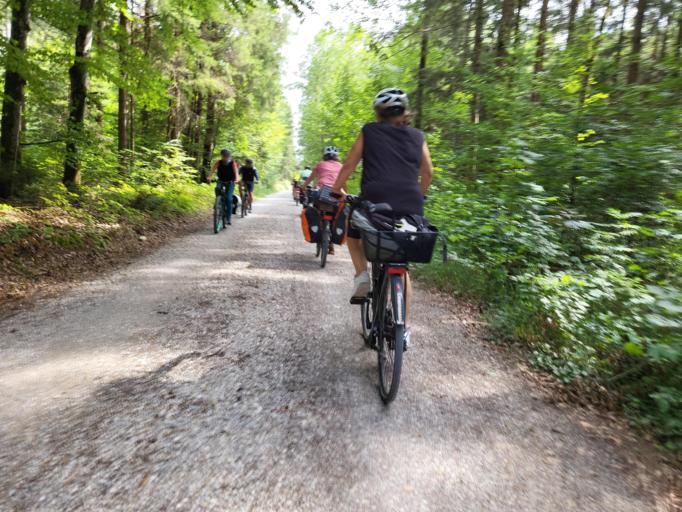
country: DE
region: Bavaria
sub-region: Upper Bavaria
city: Hohenkirchen-Siegertsbrunn
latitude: 48.0126
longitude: 11.7532
